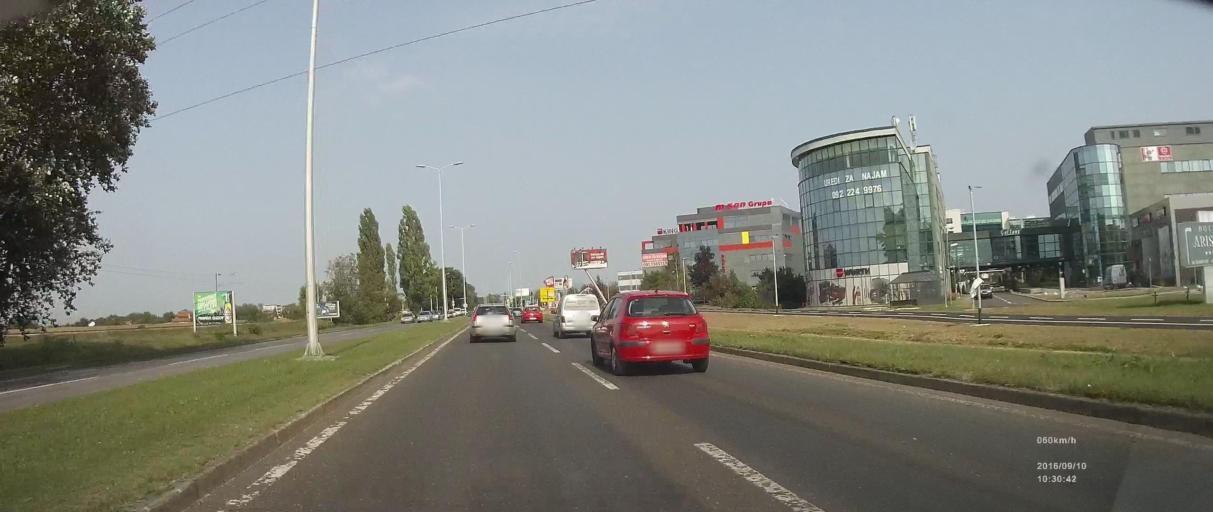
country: HR
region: Grad Zagreb
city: Odra
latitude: 45.7461
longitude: 15.9953
